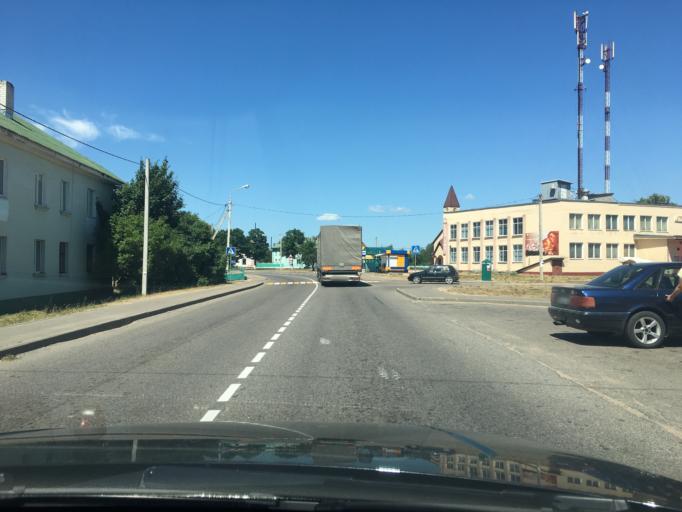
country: BY
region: Grodnenskaya
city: Iwye
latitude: 54.0319
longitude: 25.9269
